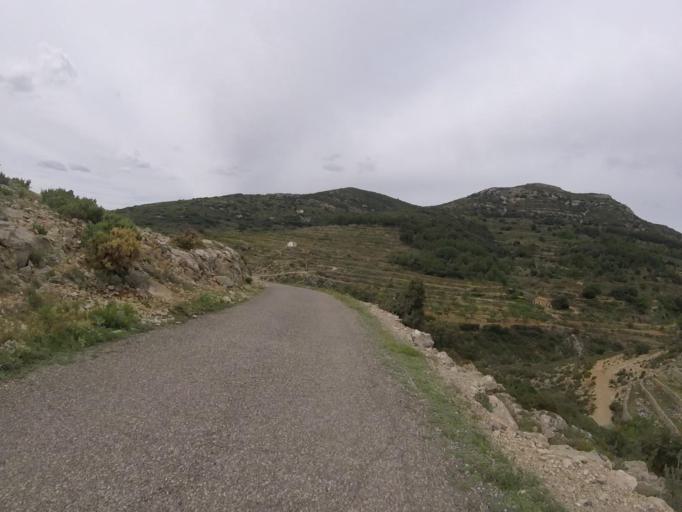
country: ES
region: Valencia
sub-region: Provincia de Castello
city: Sierra-Engarceran
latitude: 40.2646
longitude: -0.0228
